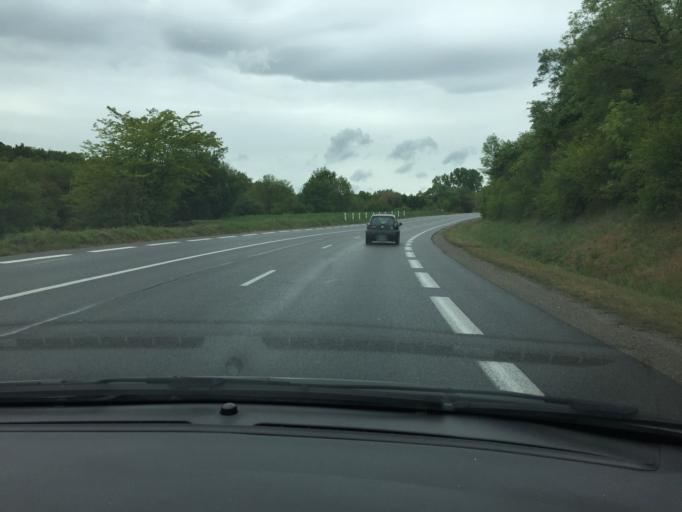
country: FR
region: Rhone-Alpes
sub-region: Departement du Rhone
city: Montagny
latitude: 45.6422
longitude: 4.7531
